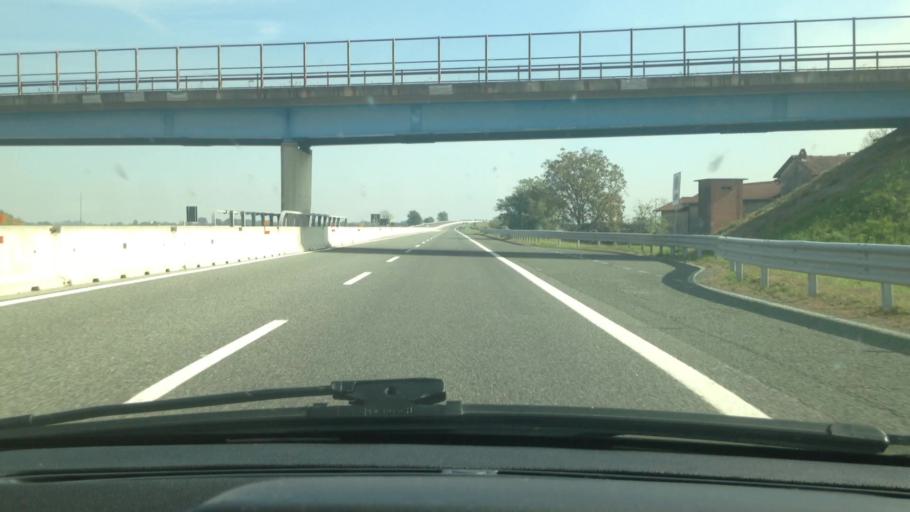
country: IT
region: Piedmont
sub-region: Provincia di Vercelli
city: Tronzano Vercellese
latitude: 45.3482
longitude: 8.1926
